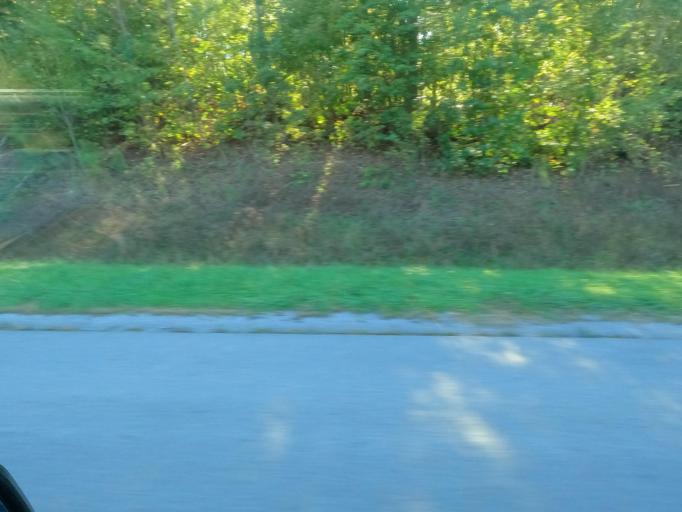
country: US
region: Tennessee
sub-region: Coffee County
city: New Union
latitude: 35.5464
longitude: -86.1857
